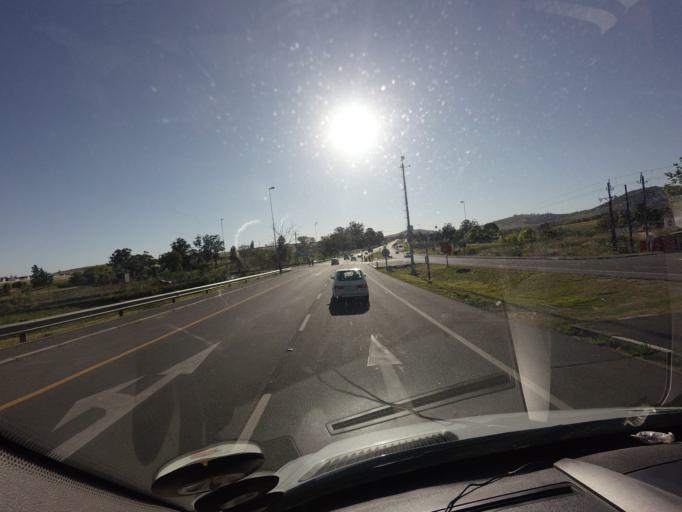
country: ZA
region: Western Cape
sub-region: Cape Winelands District Municipality
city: Stellenbosch
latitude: -33.9534
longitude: 18.7986
